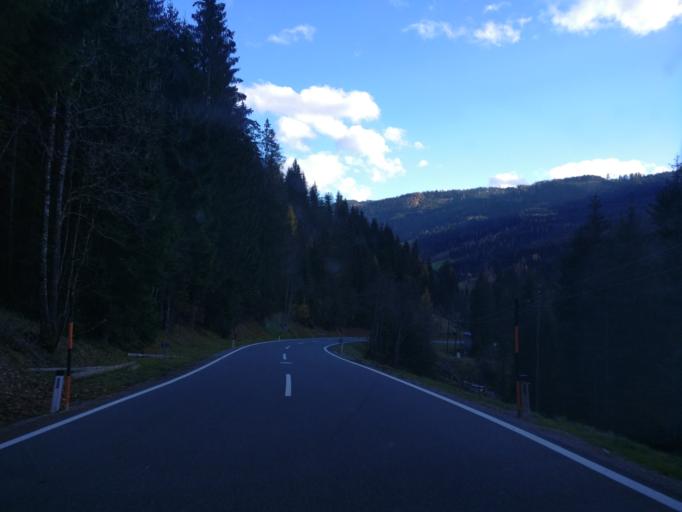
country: AT
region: Salzburg
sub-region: Politischer Bezirk Sankt Johann im Pongau
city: Muhlbach am Hochkonig
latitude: 47.3866
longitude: 13.1031
